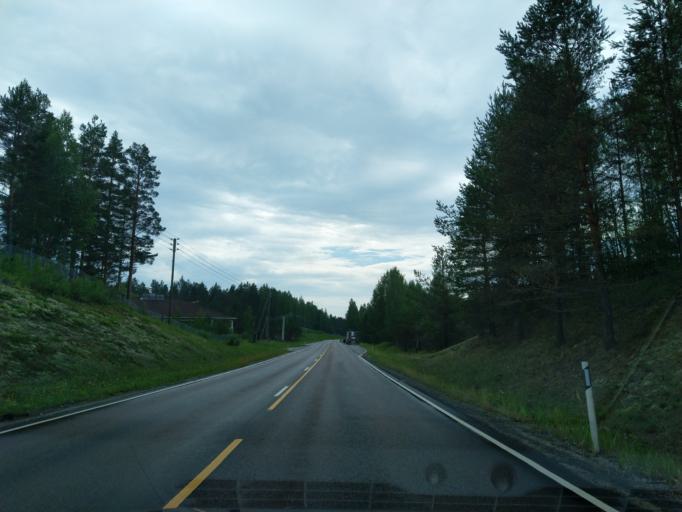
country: FI
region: Southern Savonia
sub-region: Savonlinna
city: Punkaharju
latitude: 61.6877
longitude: 29.4204
